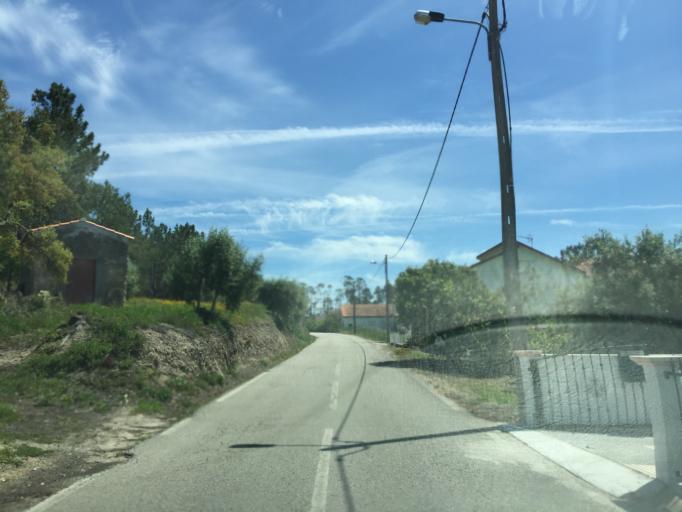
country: PT
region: Leiria
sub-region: Pombal
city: Lourical
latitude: 40.0650
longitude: -8.7167
